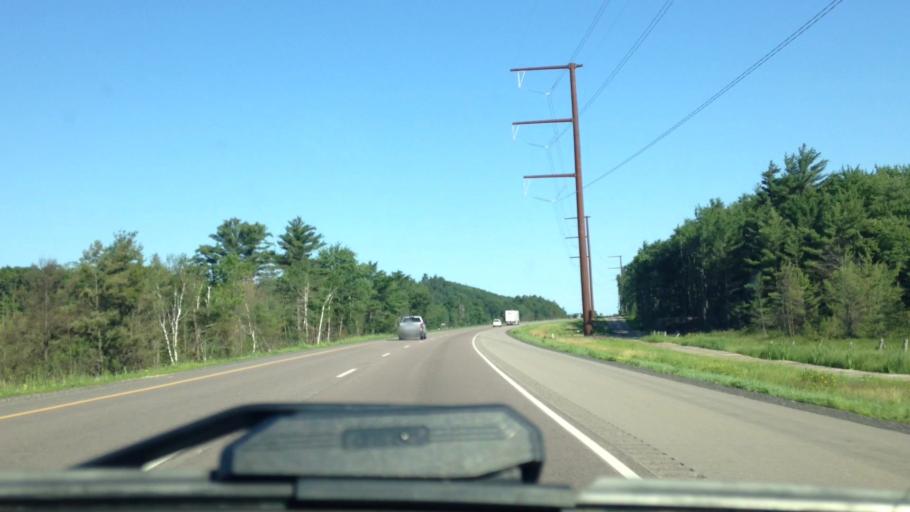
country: US
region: Wisconsin
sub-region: Monroe County
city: Tomah
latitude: 44.1578
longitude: -90.5675
